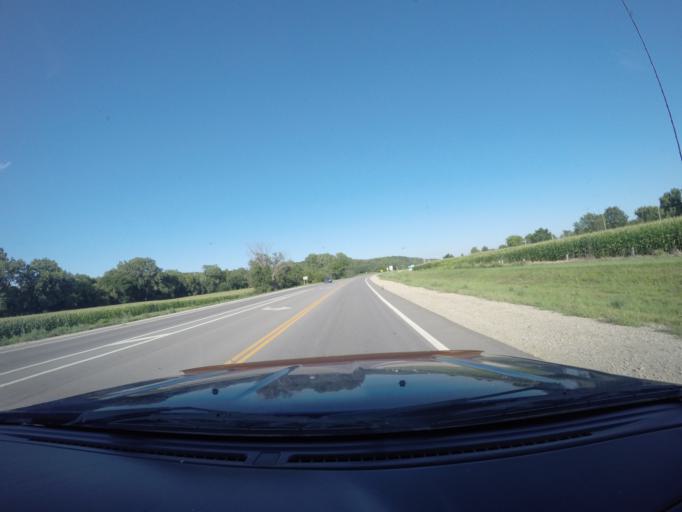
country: US
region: Kansas
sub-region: Jefferson County
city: Oskaloosa
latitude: 39.0806
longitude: -95.3902
